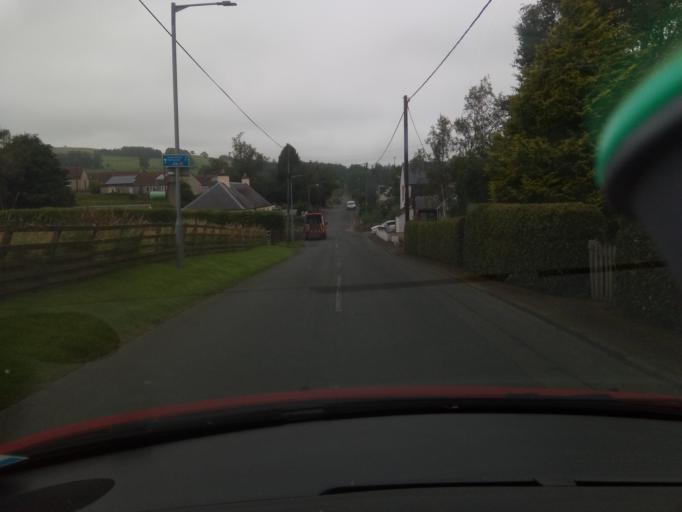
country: GB
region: Scotland
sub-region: Fife
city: Pathhead
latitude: 55.7329
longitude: -2.9076
